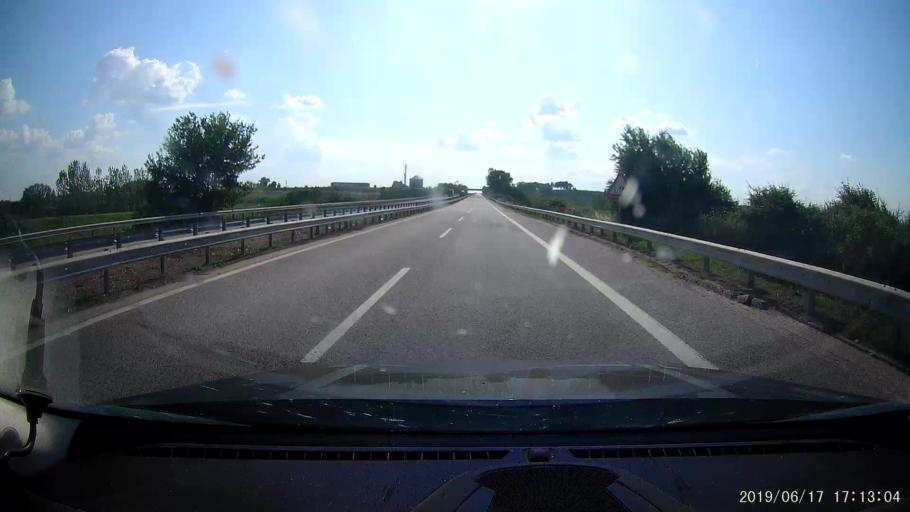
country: TR
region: Edirne
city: Edirne
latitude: 41.7013
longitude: 26.5480
